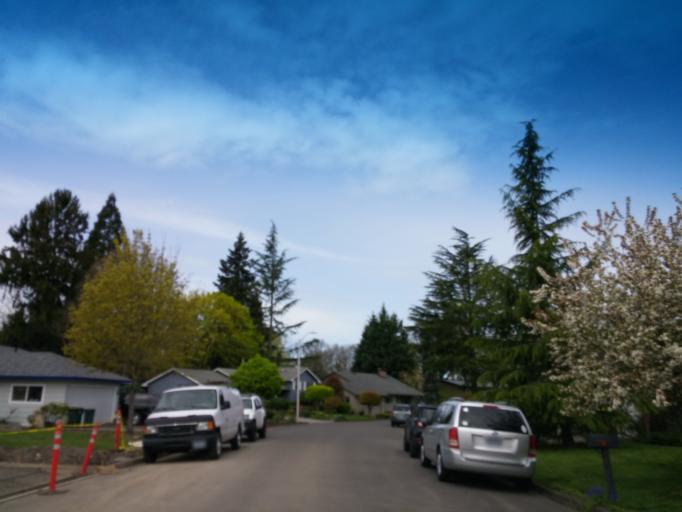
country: US
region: Oregon
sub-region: Washington County
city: Cedar Mill
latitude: 45.5299
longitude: -122.8169
